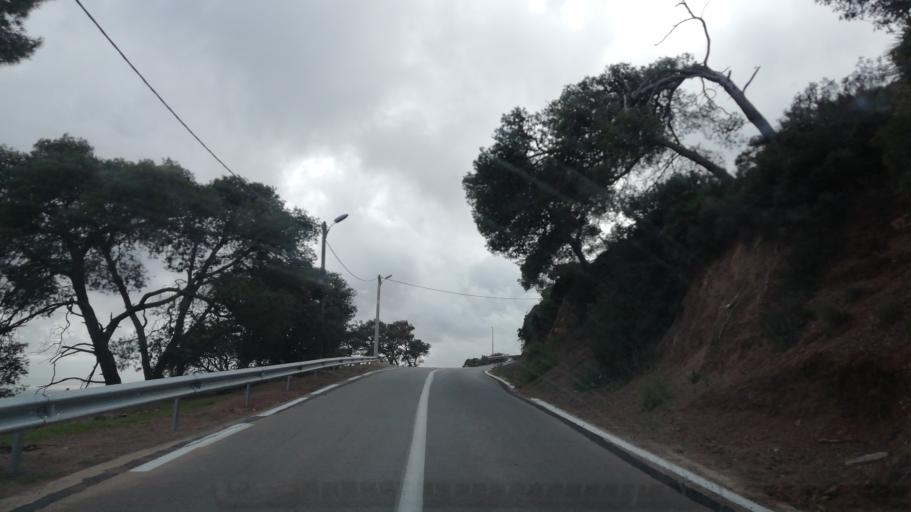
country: DZ
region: Oran
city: Oran
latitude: 35.7040
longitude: -0.6718
